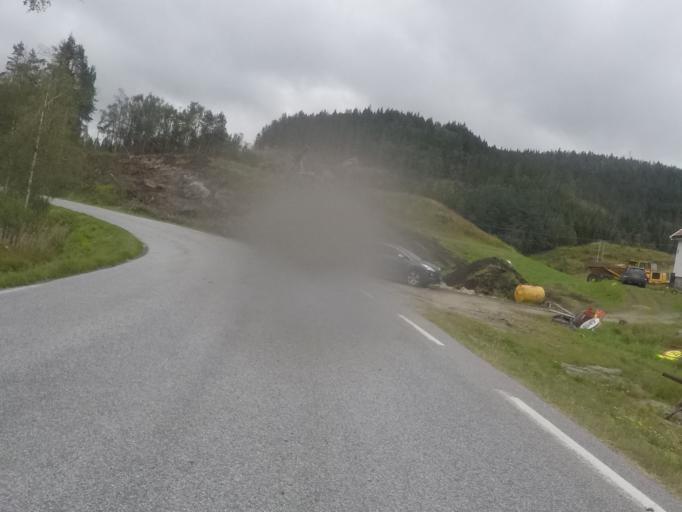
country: NO
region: Vest-Agder
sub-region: Audnedal
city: Konsmo
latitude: 58.2779
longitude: 7.3900
